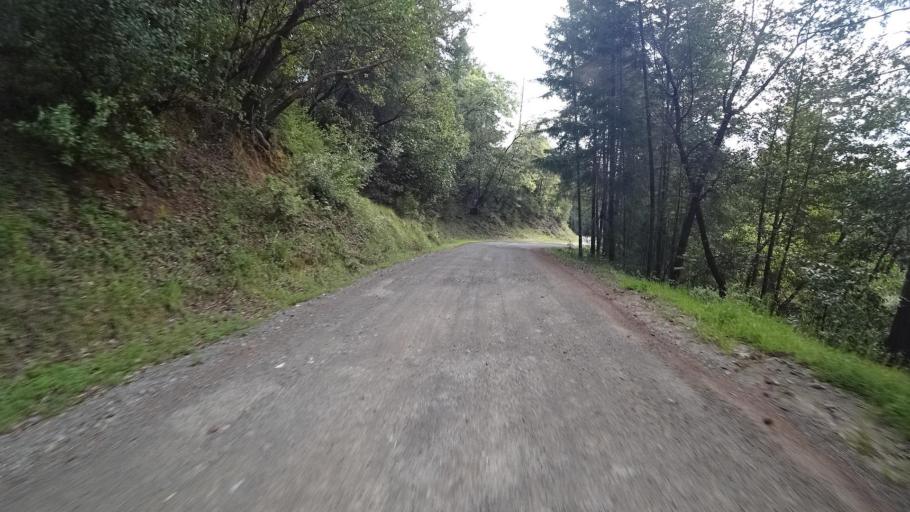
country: US
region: California
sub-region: Humboldt County
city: Redway
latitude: 40.2119
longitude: -123.6591
